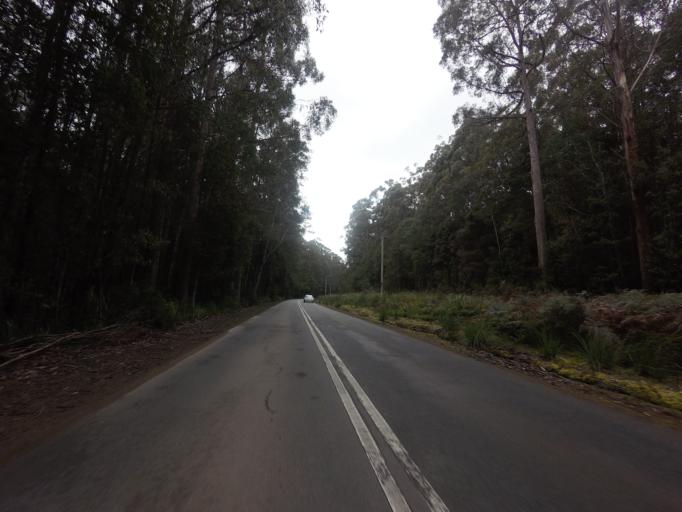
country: AU
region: Tasmania
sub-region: Huon Valley
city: Geeveston
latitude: -43.3865
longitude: 146.9620
